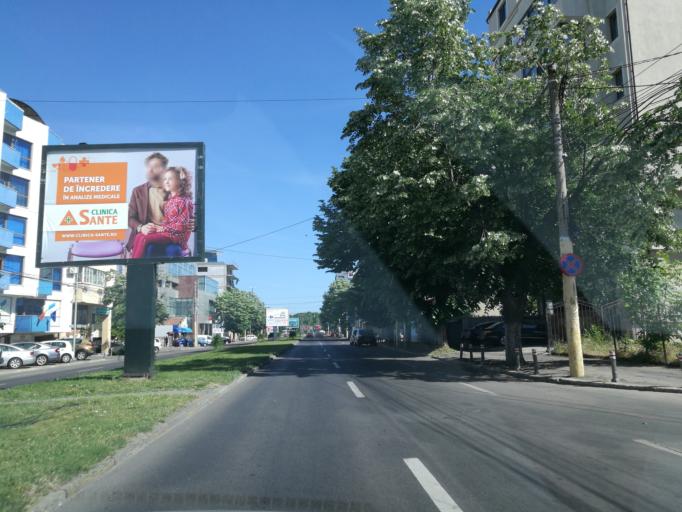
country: RO
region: Constanta
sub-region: Municipiul Constanta
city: Constanta
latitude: 44.2031
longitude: 28.6452
